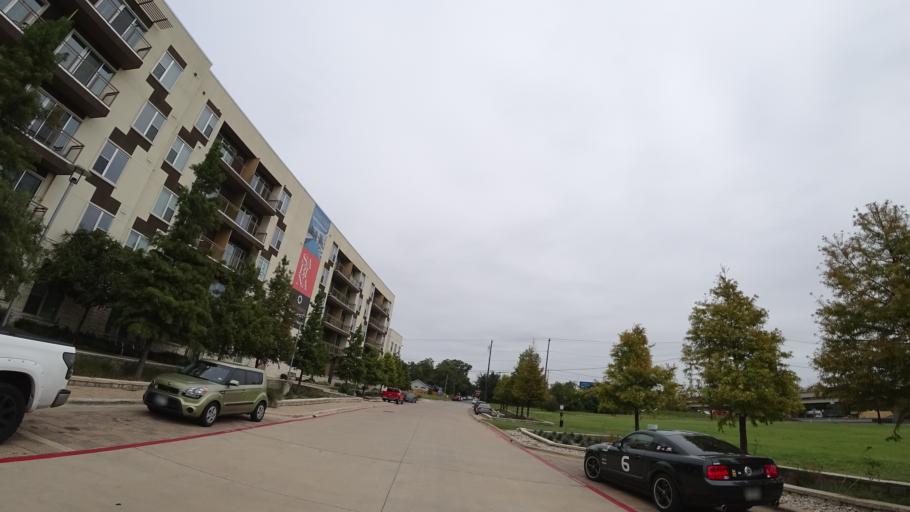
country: US
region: Texas
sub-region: Travis County
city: Austin
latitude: 30.2926
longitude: -97.7223
